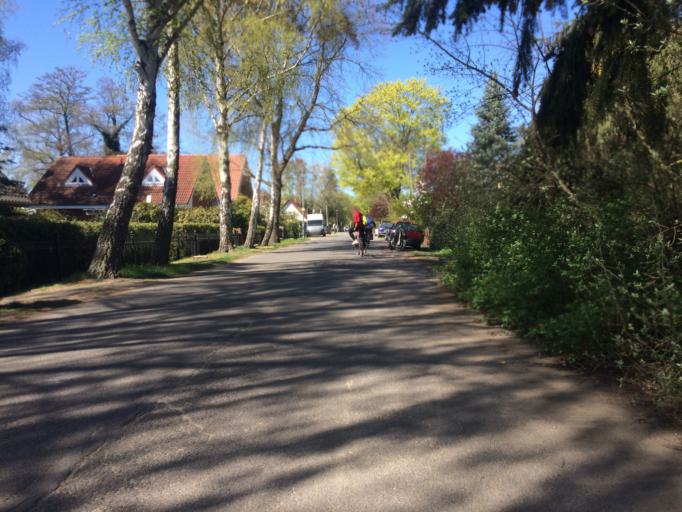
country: DE
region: Berlin
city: Rahnsdorf
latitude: 52.4363
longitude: 13.6880
